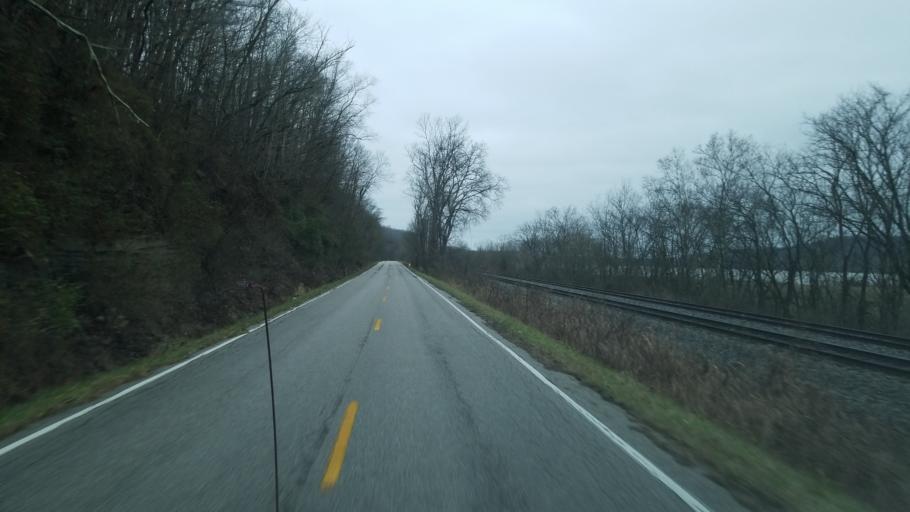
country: US
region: Kentucky
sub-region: Bracken County
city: Augusta
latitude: 38.7671
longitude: -84.0334
